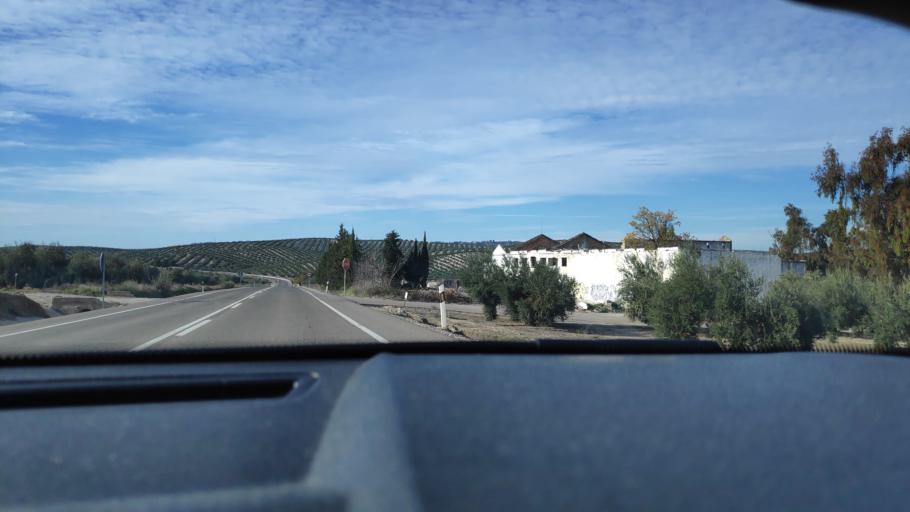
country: ES
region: Andalusia
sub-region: Provincia de Jaen
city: Higuera de Calatrava
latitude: 37.8482
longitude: -4.1267
